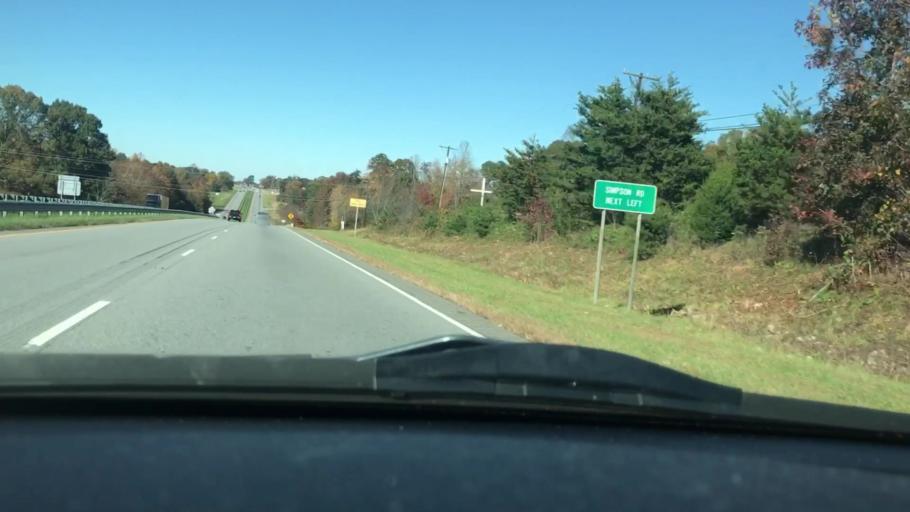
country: US
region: North Carolina
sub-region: Guilford County
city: Stokesdale
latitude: 36.2988
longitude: -79.9405
